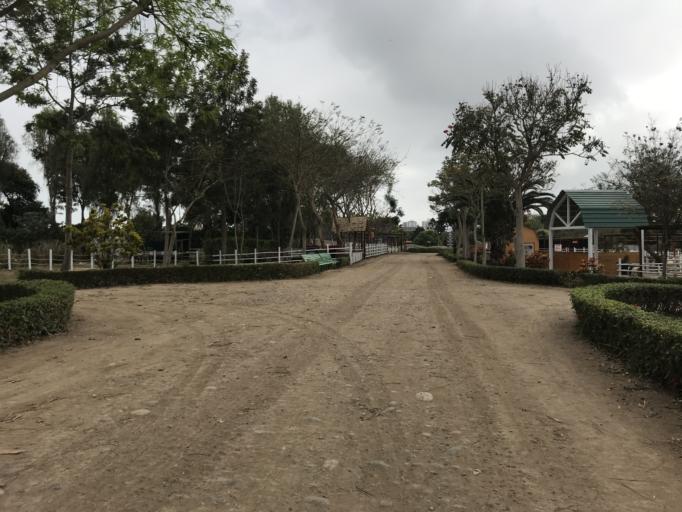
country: PE
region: Callao
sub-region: Callao
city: Callao
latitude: -12.0663
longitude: -77.0858
